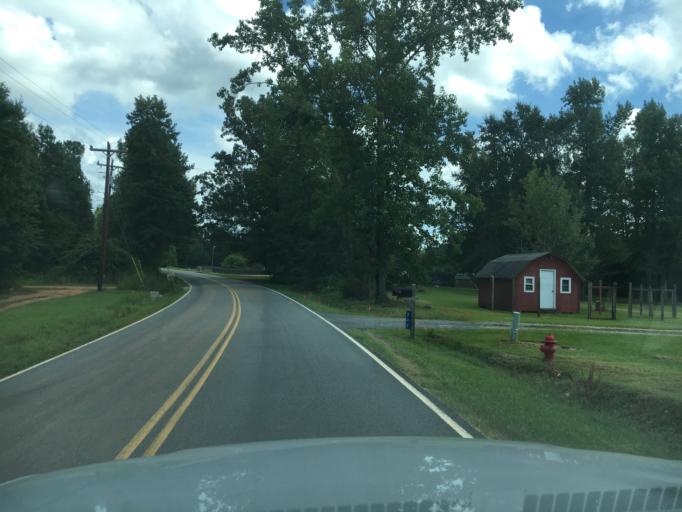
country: US
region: South Carolina
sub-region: Anderson County
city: Belton
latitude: 34.5506
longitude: -82.4635
